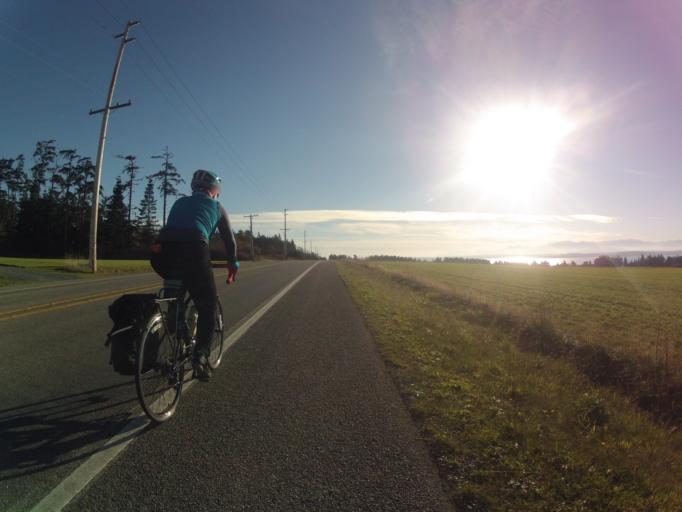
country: US
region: Washington
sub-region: Island County
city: Coupeville
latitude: 48.1853
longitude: -122.6881
